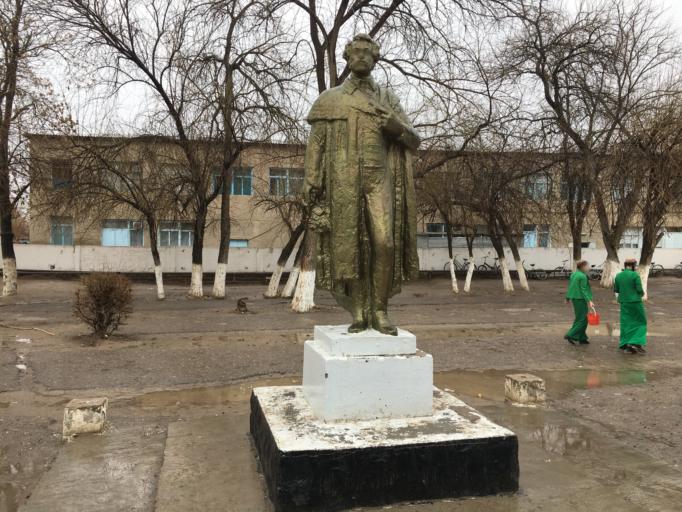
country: TM
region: Mary
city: Yoloeten
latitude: 37.2974
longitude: 62.3626
